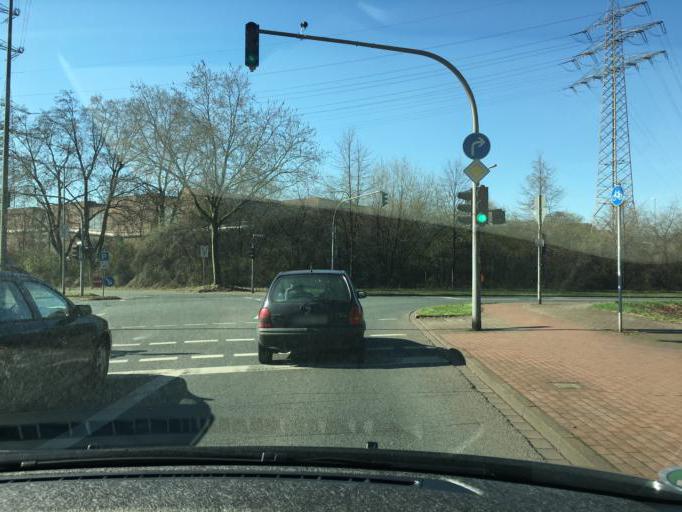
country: DE
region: North Rhine-Westphalia
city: Meiderich
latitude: 51.5032
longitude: 6.7424
